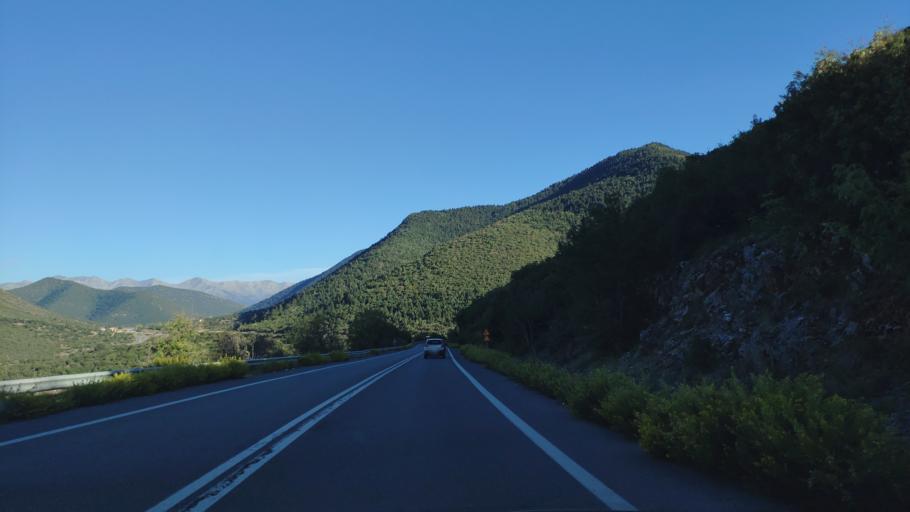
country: GR
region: Peloponnese
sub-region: Nomos Arkadias
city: Langadhia
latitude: 37.7271
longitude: 22.2089
